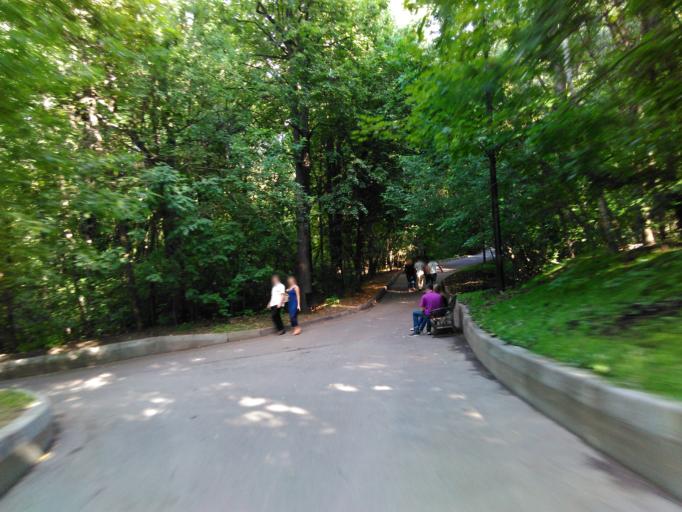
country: RU
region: Moscow
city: Luzhniki
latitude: 55.7092
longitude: 37.5584
